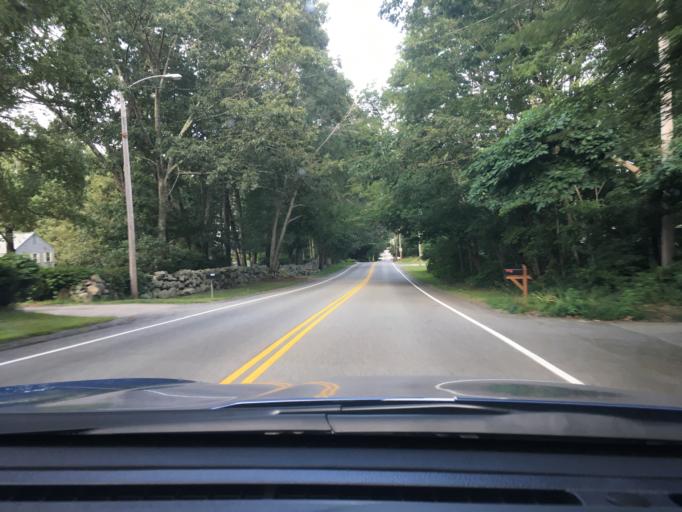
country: US
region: Rhode Island
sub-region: Kent County
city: East Greenwich
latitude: 41.6448
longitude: -71.5015
